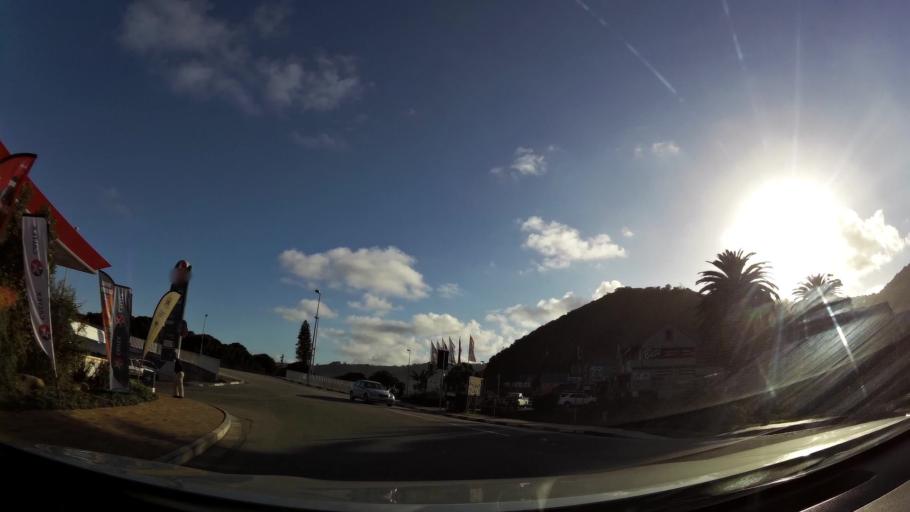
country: ZA
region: Western Cape
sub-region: Eden District Municipality
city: George
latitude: -33.9938
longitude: 22.5748
